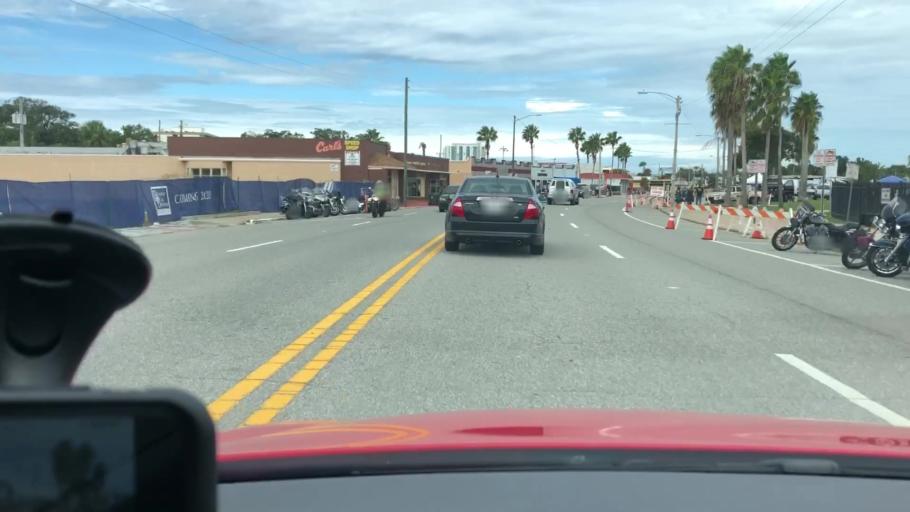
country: US
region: Florida
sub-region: Volusia County
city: Daytona Beach
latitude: 29.2187
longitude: -81.0224
